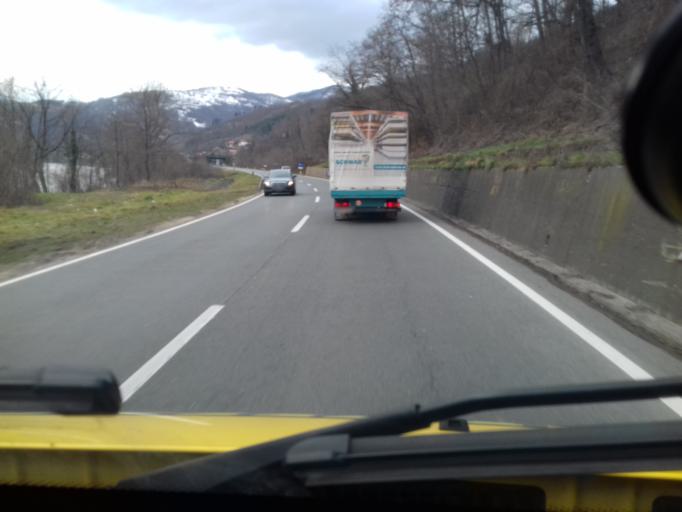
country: BA
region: Federation of Bosnia and Herzegovina
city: Zeljezno Polje
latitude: 44.3565
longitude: 17.9565
